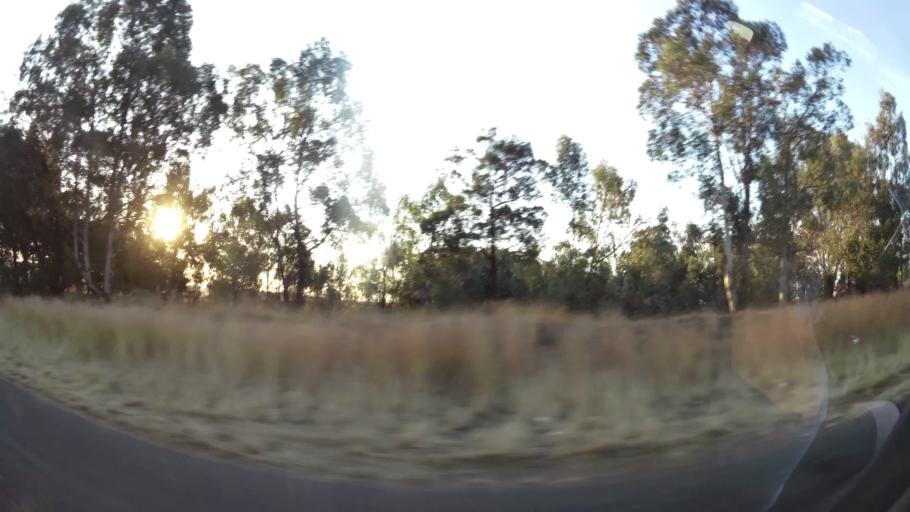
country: ZA
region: Gauteng
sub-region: West Rand District Municipality
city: Randfontein
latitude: -26.2035
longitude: 27.6677
